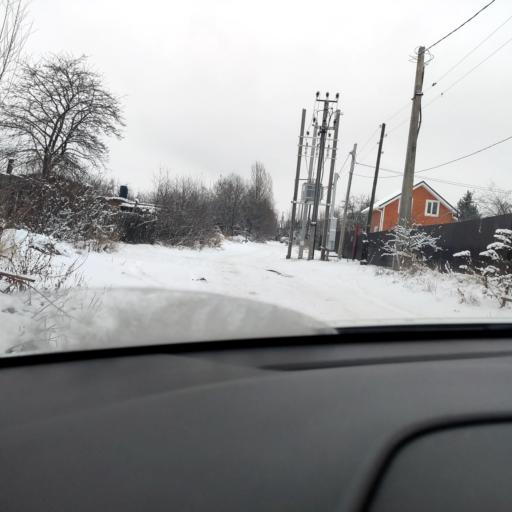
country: RU
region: Tatarstan
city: Vysokaya Gora
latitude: 55.8407
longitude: 49.2221
